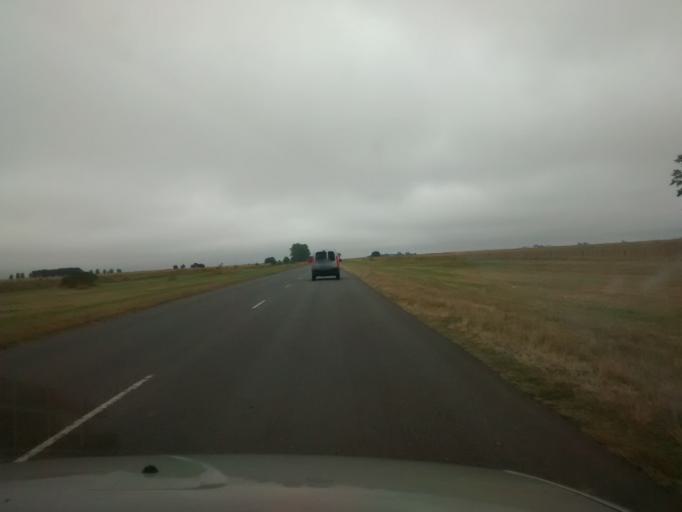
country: AR
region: Buenos Aires
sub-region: Partido de Ayacucho
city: Ayacucho
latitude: -37.2322
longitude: -58.4938
